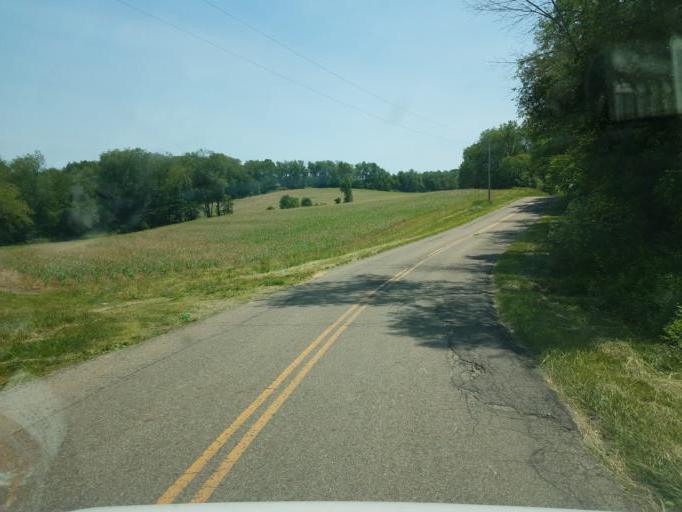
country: US
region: Ohio
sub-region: Knox County
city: Danville
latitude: 40.4747
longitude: -82.3410
